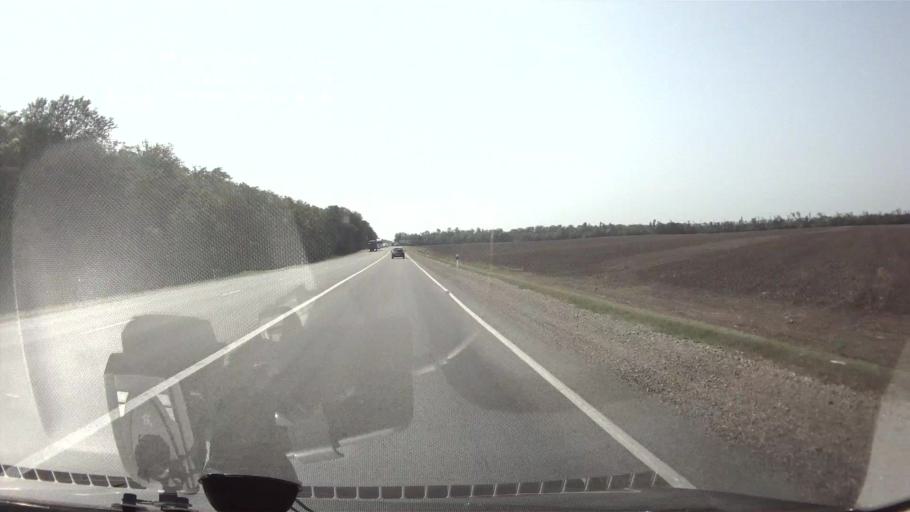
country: RU
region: Krasnodarskiy
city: Vasyurinskaya
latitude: 45.1490
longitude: 39.4381
